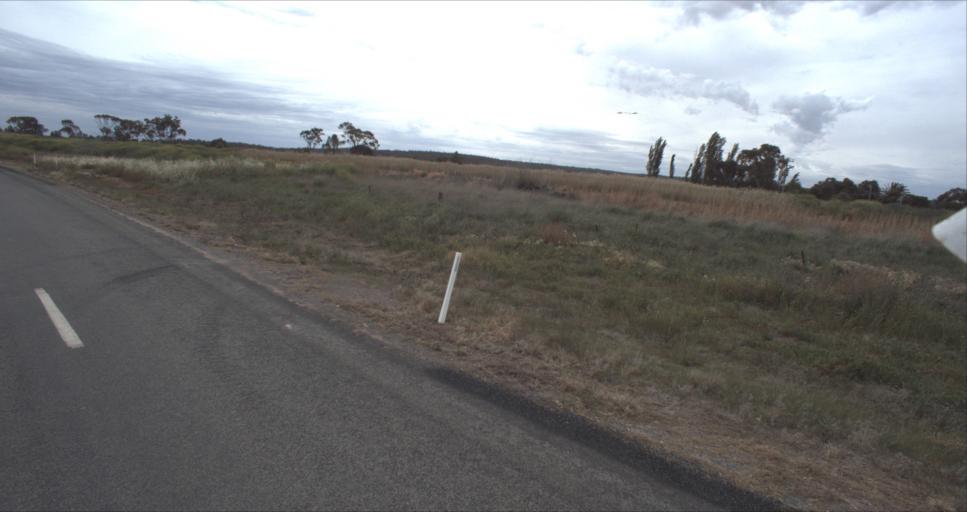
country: AU
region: New South Wales
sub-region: Leeton
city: Leeton
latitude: -34.4502
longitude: 146.3883
